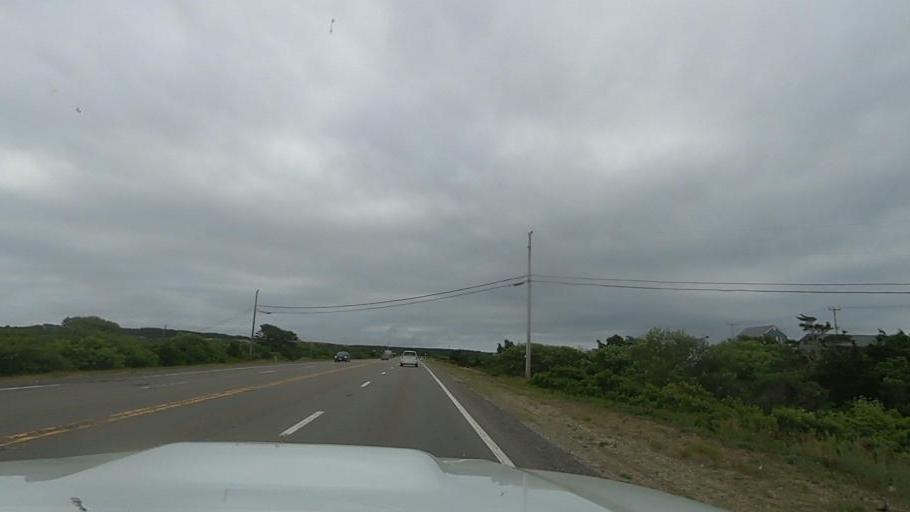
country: US
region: Massachusetts
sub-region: Barnstable County
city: Provincetown
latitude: 42.0525
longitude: -70.1222
